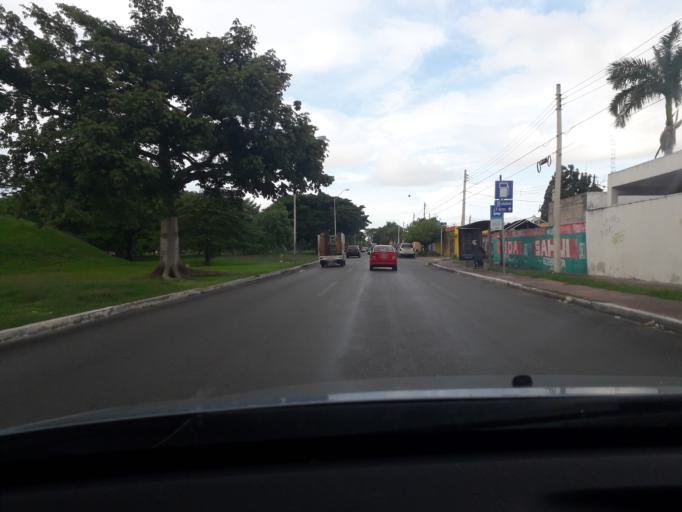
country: MX
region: Yucatan
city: Merida
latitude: 20.9806
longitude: -89.6633
